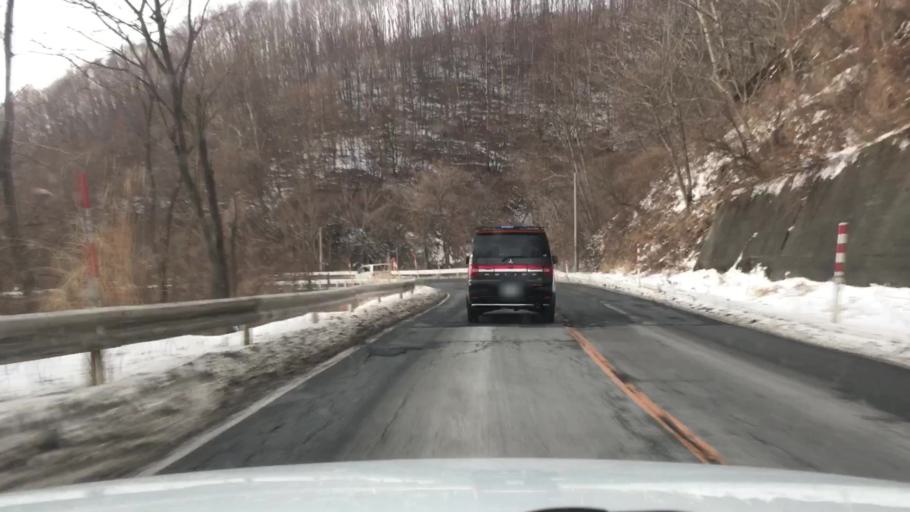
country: JP
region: Iwate
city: Morioka-shi
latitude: 39.6608
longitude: 141.3350
